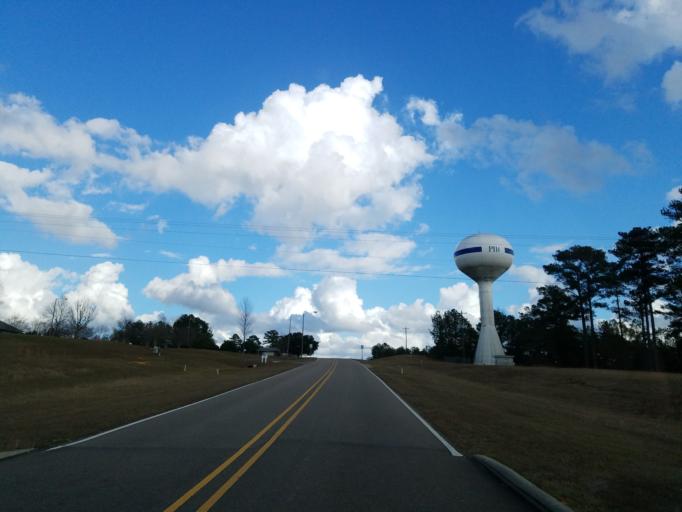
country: US
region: Mississippi
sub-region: Forrest County
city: Rawls Springs
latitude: 31.4693
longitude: -89.3319
